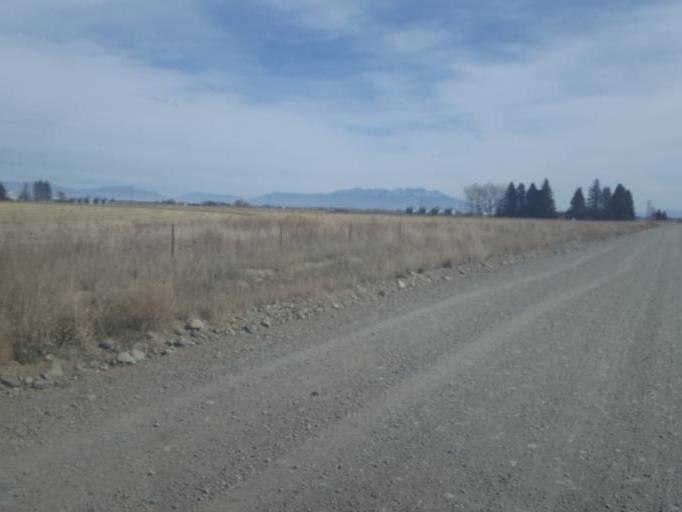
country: US
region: Colorado
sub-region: Rio Grande County
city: Monte Vista
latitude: 37.4010
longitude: -106.0794
